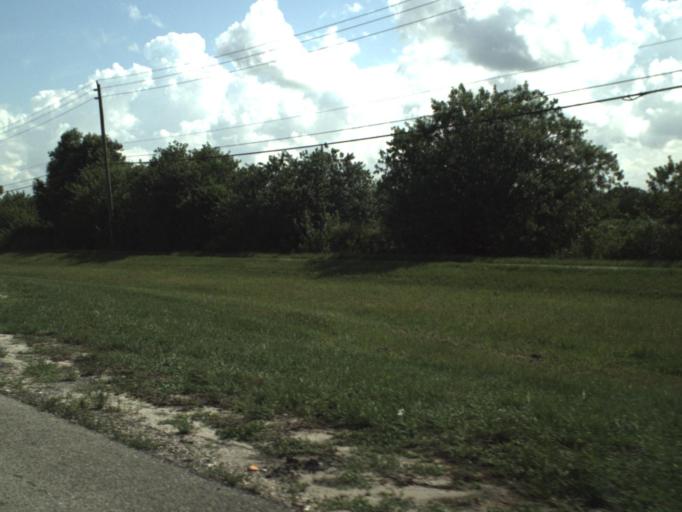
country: US
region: Florida
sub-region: Palm Beach County
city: Villages of Oriole
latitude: 26.5216
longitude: -80.2055
